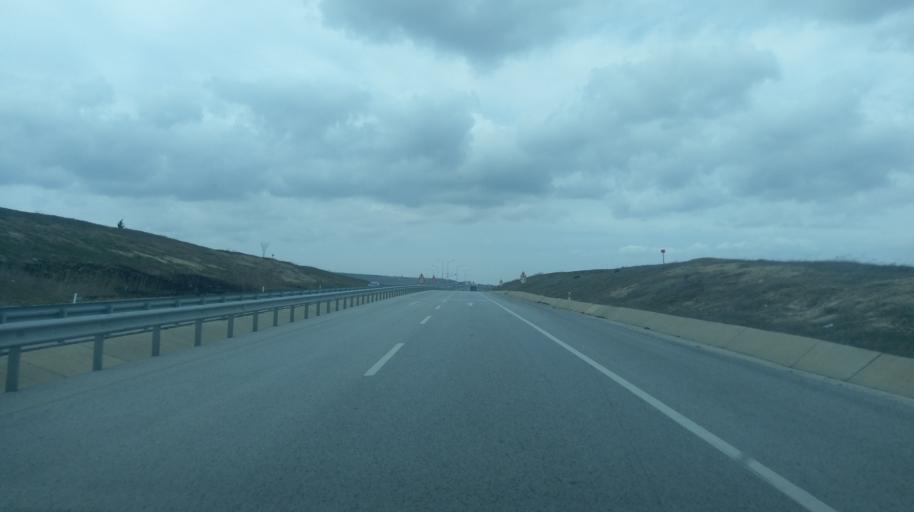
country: TR
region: Edirne
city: Uzun Keupru
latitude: 41.2714
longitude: 26.7101
